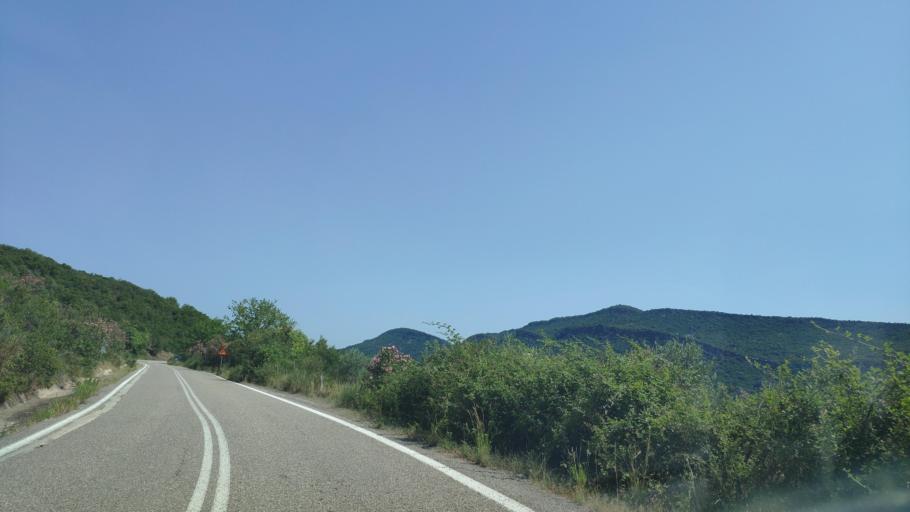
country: GR
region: West Greece
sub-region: Nomos Aitolias kai Akarnanias
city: Lepenou
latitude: 38.7637
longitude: 21.3376
